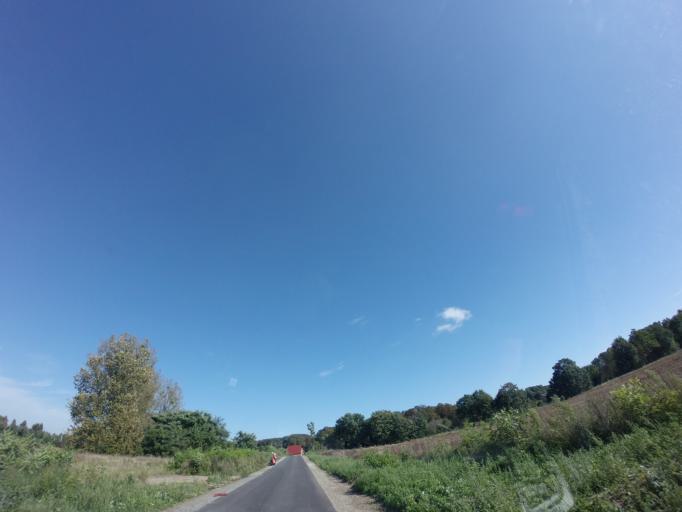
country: PL
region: West Pomeranian Voivodeship
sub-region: Powiat choszczenski
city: Recz
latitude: 53.1887
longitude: 15.5050
